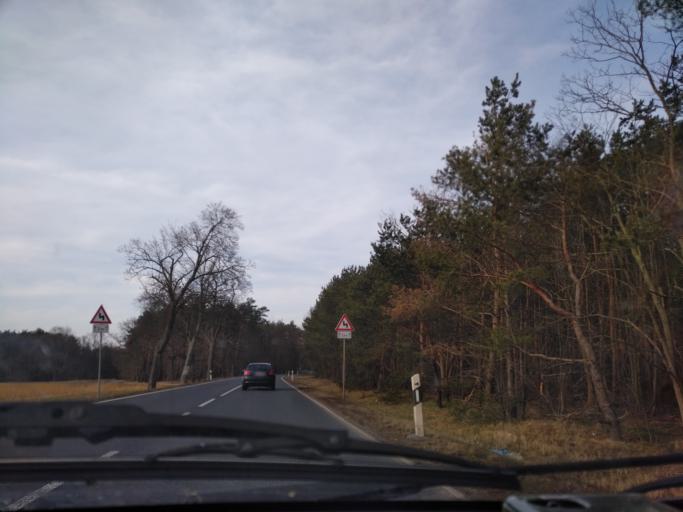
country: DE
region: Brandenburg
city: Herzberg
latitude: 51.7179
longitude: 13.2316
